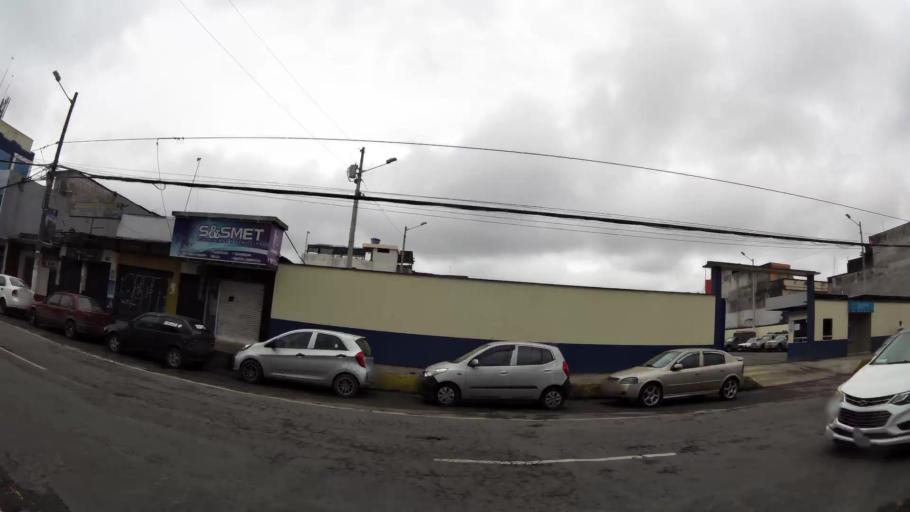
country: EC
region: Santo Domingo de los Tsachilas
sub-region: Canton Santo Domingo de los Colorados
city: Santo Domingo de los Colorados
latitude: -0.2478
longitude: -79.1683
